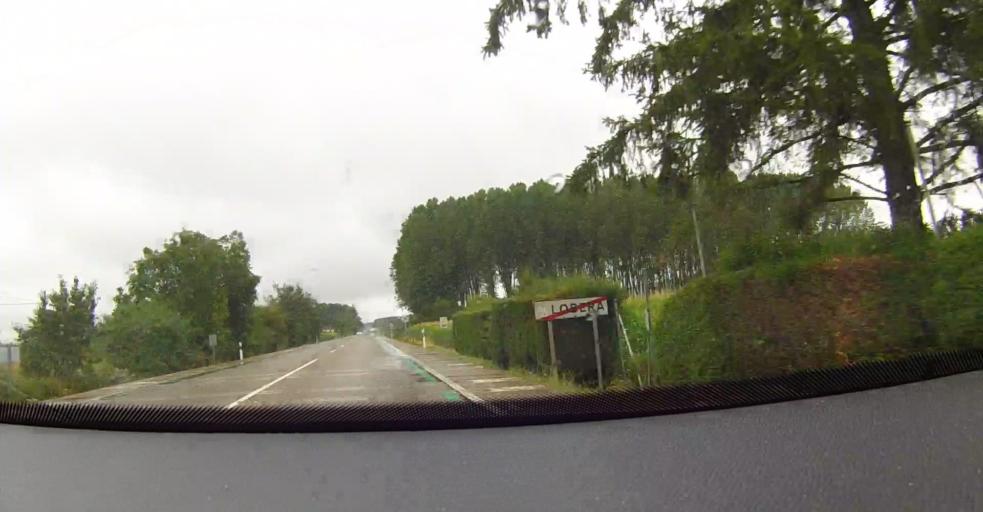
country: ES
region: Castille and Leon
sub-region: Provincia de Palencia
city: Saldana
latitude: 42.5003
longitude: -4.7306
